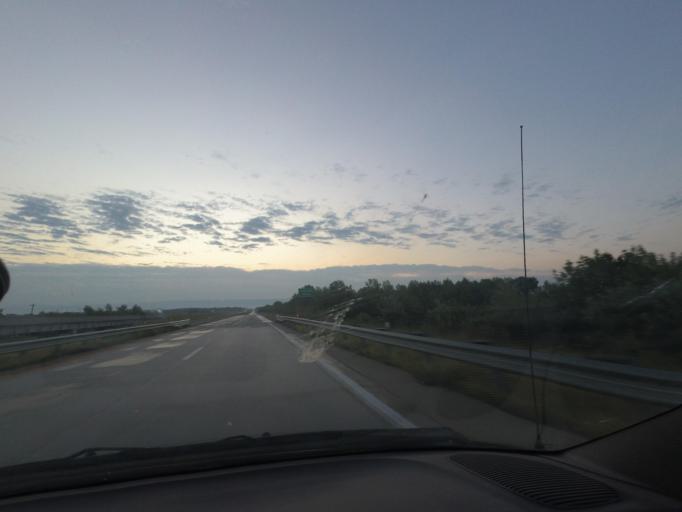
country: US
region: Missouri
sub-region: Macon County
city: Macon
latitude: 39.7601
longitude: -92.6928
